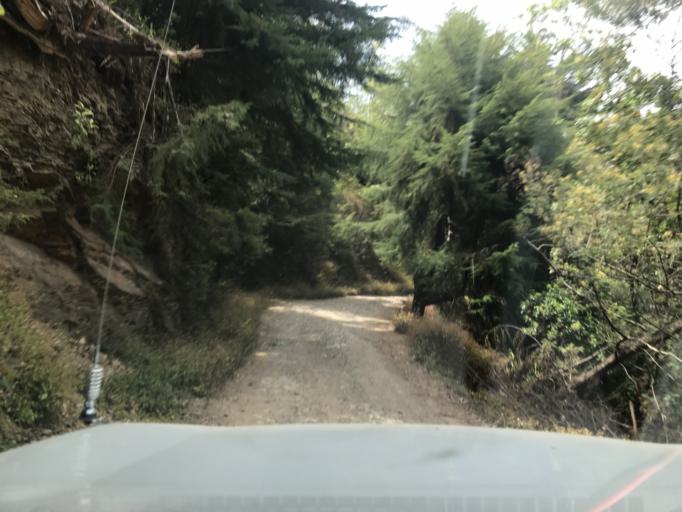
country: TL
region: Ainaro
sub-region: Ainaro
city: Ainaro
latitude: -8.8813
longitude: 125.5296
